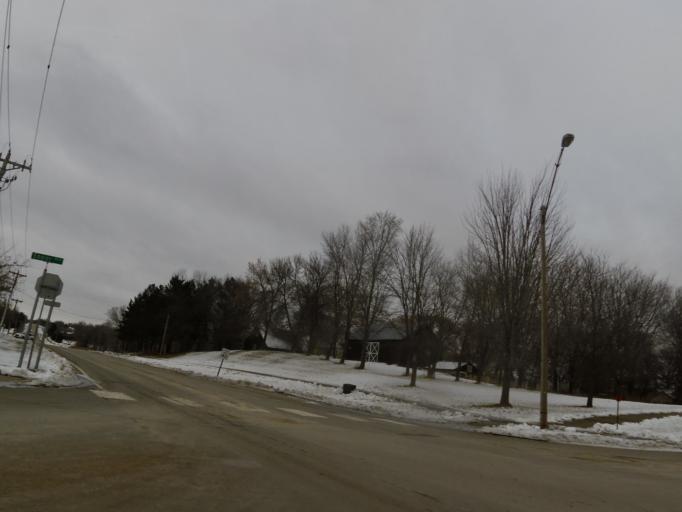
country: US
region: Minnesota
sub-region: Carver County
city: Chaska
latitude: 44.8057
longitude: -93.6121
